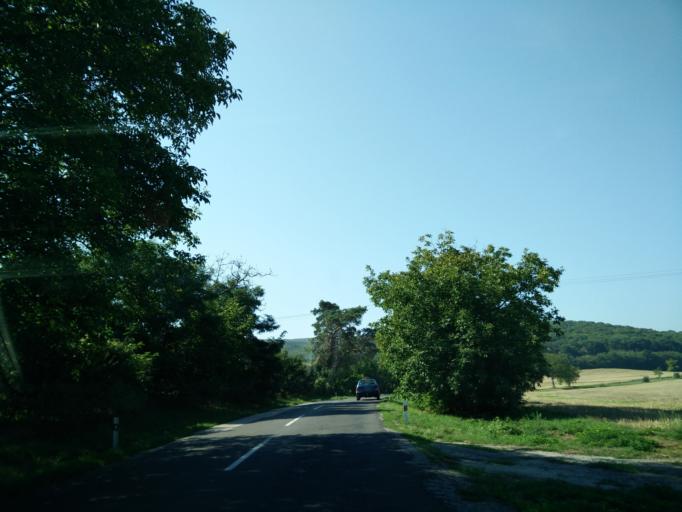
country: SK
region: Nitriansky
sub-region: Okres Nitra
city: Nitra
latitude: 48.3736
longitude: 18.0905
